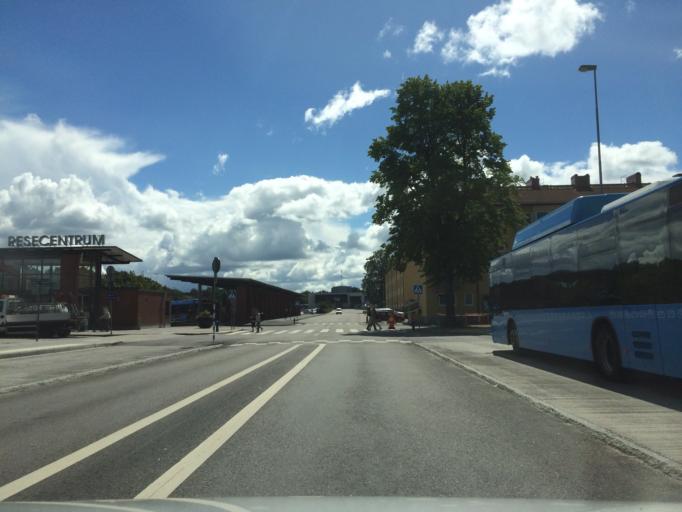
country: SE
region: Vaestra Goetaland
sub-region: Trollhattan
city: Trollhattan
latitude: 58.2873
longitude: 12.2978
